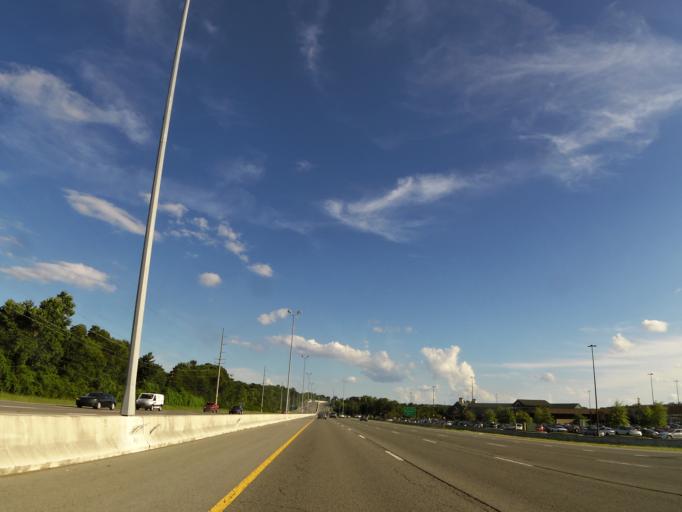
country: US
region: Tennessee
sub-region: Davidson County
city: Lakewood
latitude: 36.2045
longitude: -86.6898
